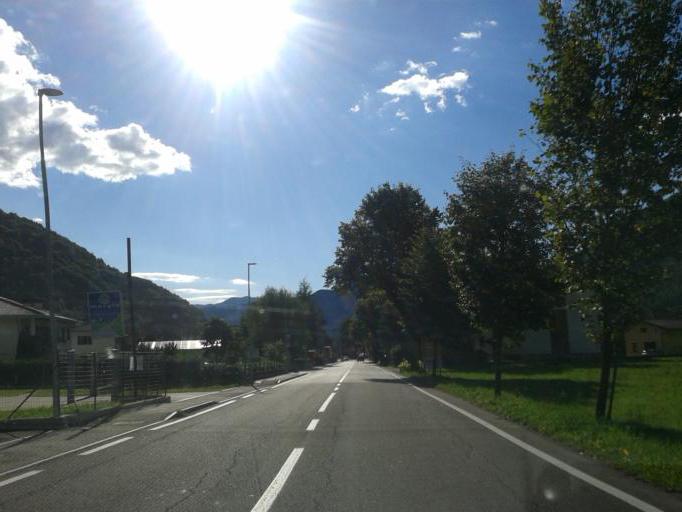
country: IT
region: Trentino-Alto Adige
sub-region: Provincia di Trento
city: Pieve di Ledro
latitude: 45.8914
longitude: 10.7265
